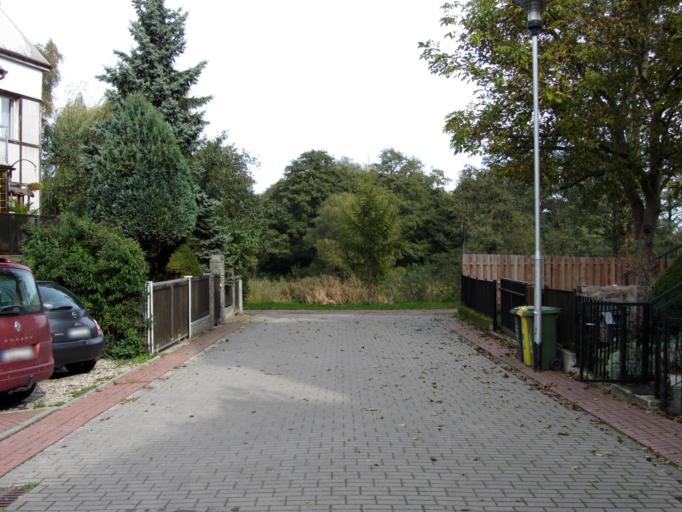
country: PL
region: West Pomeranian Voivodeship
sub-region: Powiat kolobrzeski
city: Kolobrzeg
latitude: 54.1713
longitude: 15.5766
